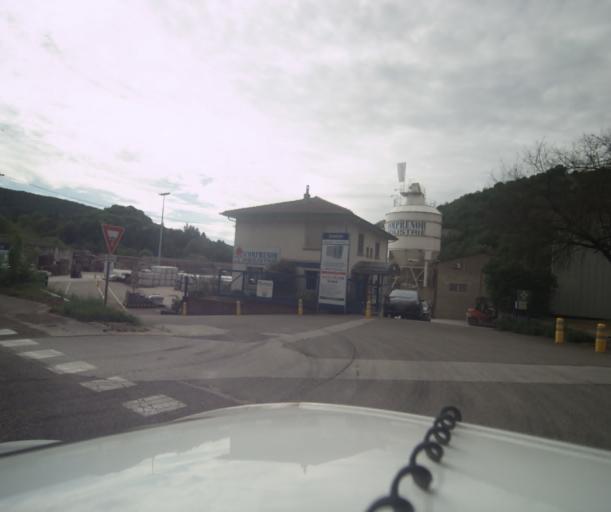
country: FR
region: Franche-Comte
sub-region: Departement du Doubs
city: Beure
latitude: 47.2144
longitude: 6.0040
